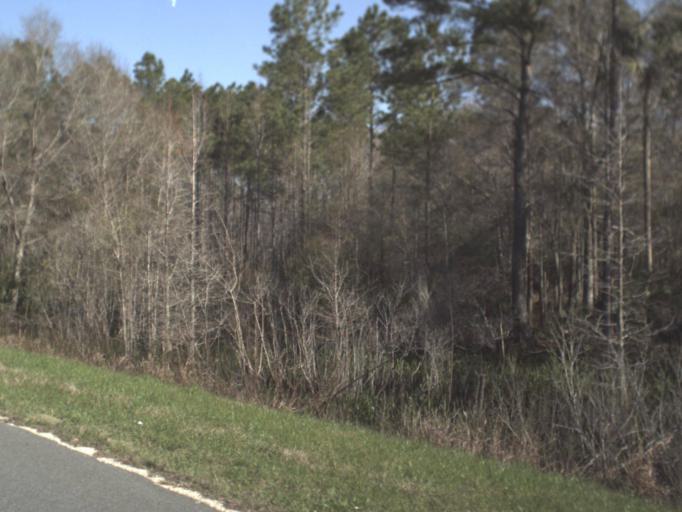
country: US
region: Florida
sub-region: Leon County
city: Woodville
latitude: 30.1815
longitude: -84.0130
